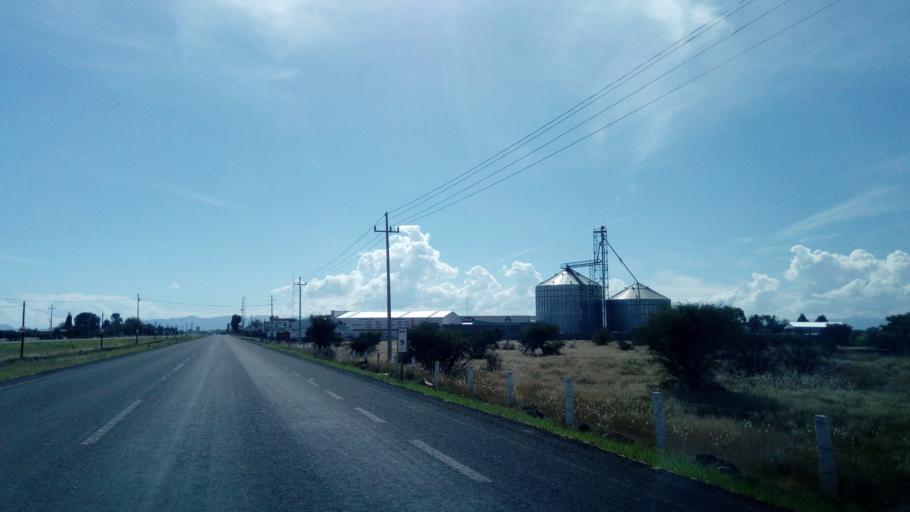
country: MX
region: Durango
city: Victoria de Durango
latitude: 24.0860
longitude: -104.5629
